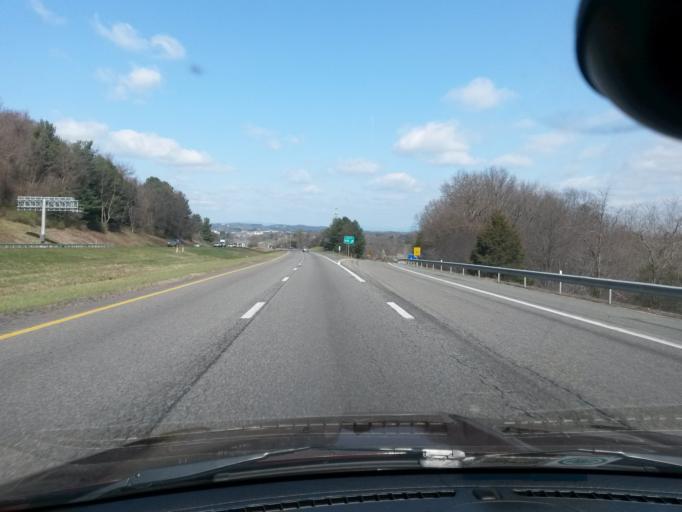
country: US
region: Virginia
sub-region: City of Waynesboro
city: Waynesboro
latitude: 38.0448
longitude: -78.9019
